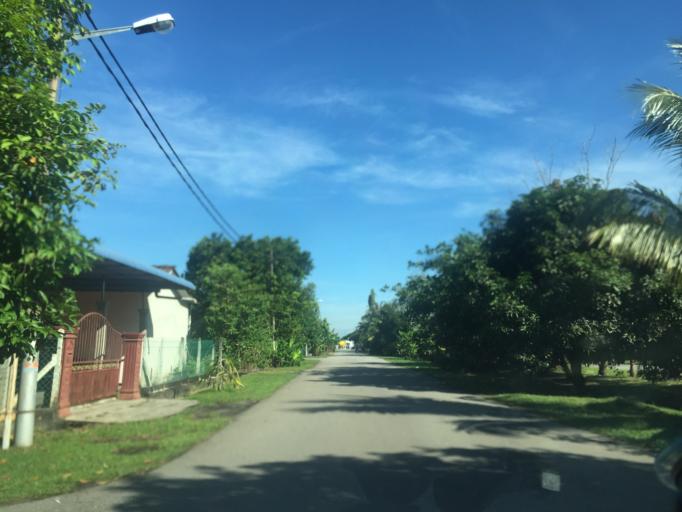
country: MY
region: Penang
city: Tasek Glugor
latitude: 5.5125
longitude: 100.5456
